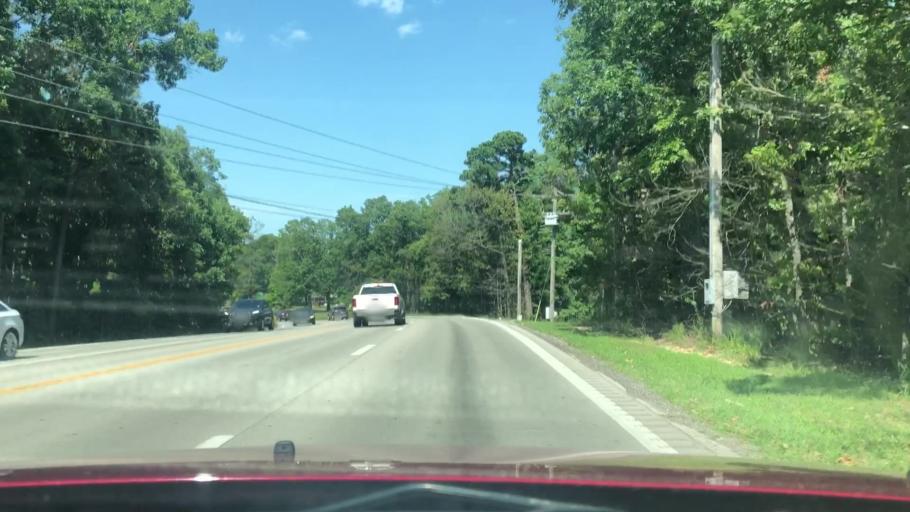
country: US
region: Missouri
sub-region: Stone County
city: Kimberling City
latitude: 36.6722
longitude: -93.3312
